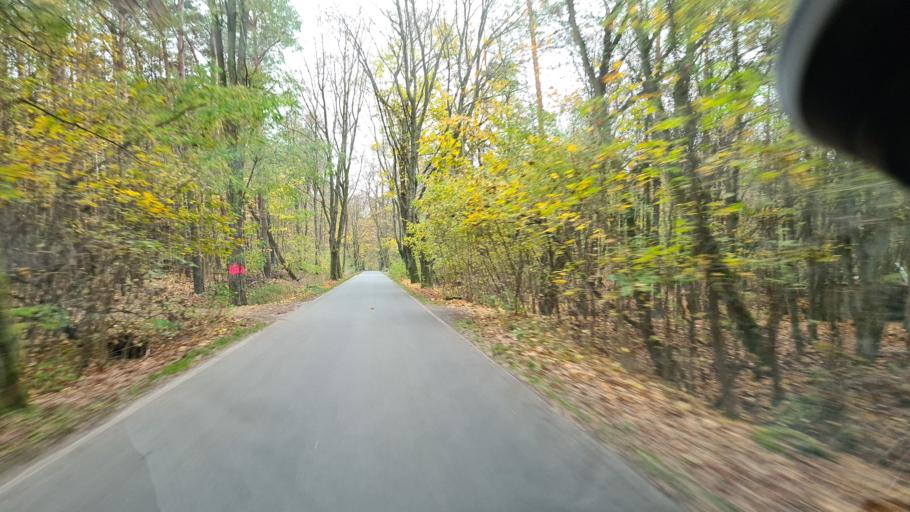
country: DE
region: Brandenburg
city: Lindow
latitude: 52.9581
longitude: 12.9850
